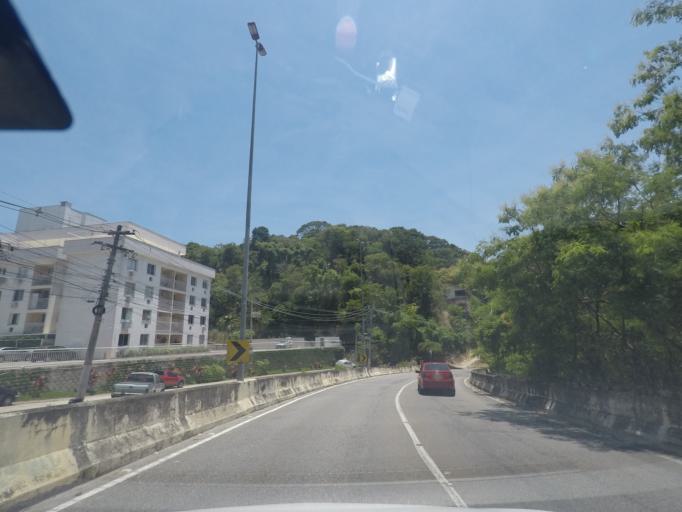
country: BR
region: Rio de Janeiro
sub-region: Niteroi
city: Niteroi
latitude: -22.9200
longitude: -43.0636
